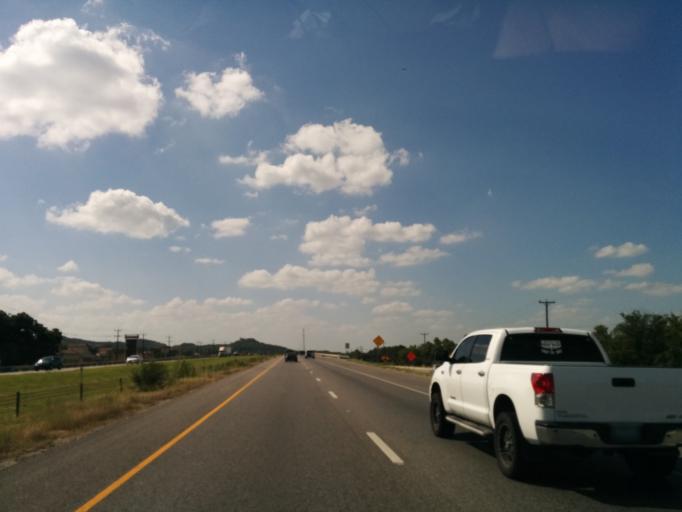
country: US
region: Texas
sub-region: Bexar County
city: Cross Mountain
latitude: 29.6452
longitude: -98.6203
